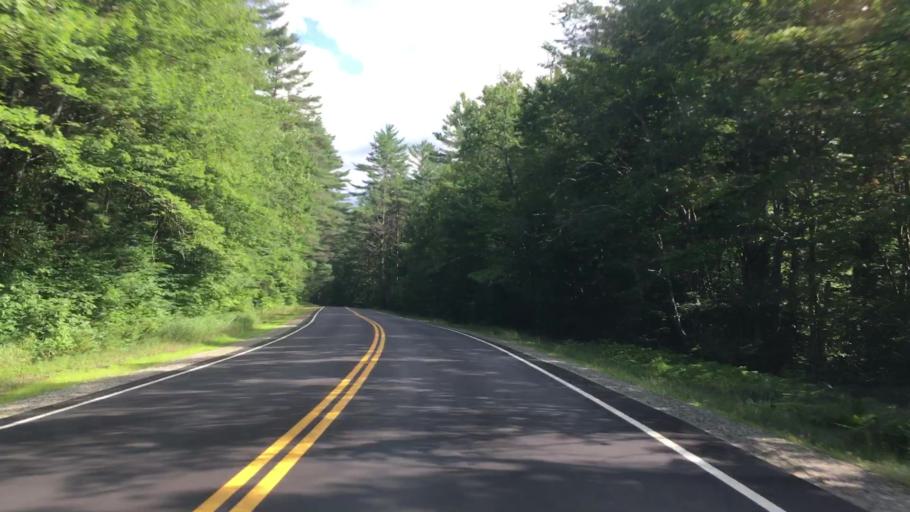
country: US
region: New Hampshire
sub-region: Grafton County
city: North Haverhill
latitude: 44.1042
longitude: -71.8663
